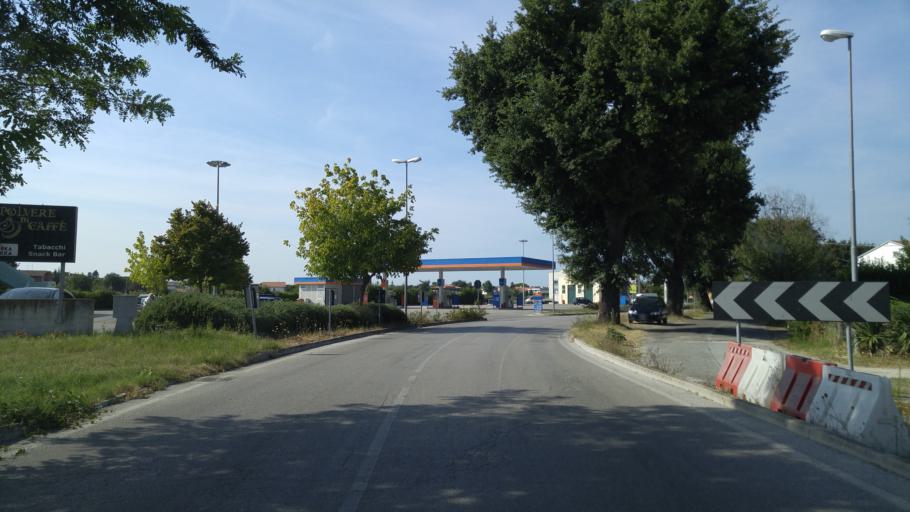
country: IT
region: The Marches
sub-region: Provincia di Pesaro e Urbino
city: Rosciano
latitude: 43.8211
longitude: 13.0095
